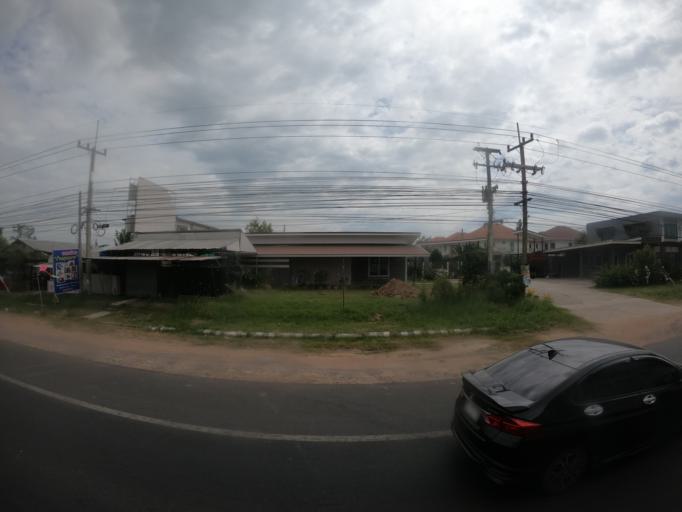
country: TH
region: Maha Sarakham
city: Maha Sarakham
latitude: 16.2515
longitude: 103.2756
